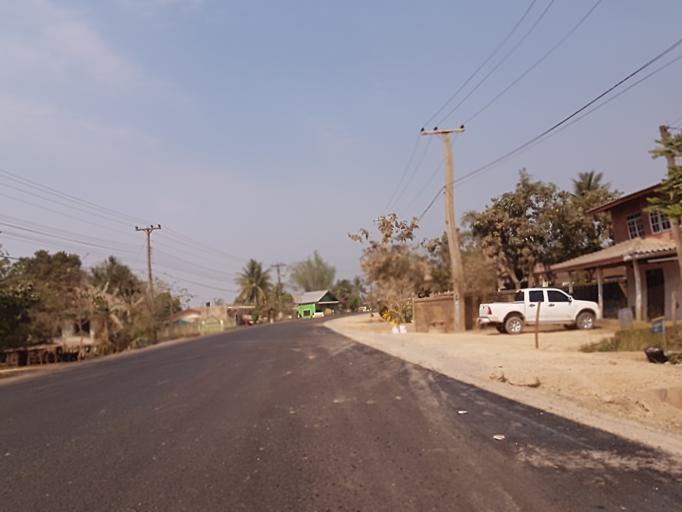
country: TH
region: Nong Khai
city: Nong Khai
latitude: 17.9263
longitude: 102.7702
